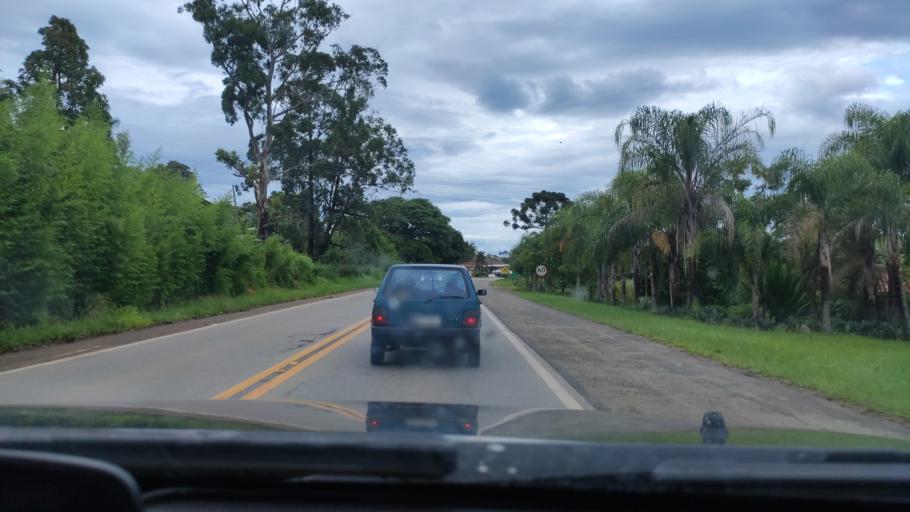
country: BR
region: Sao Paulo
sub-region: Braganca Paulista
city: Braganca Paulista
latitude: -22.8957
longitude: -46.5428
